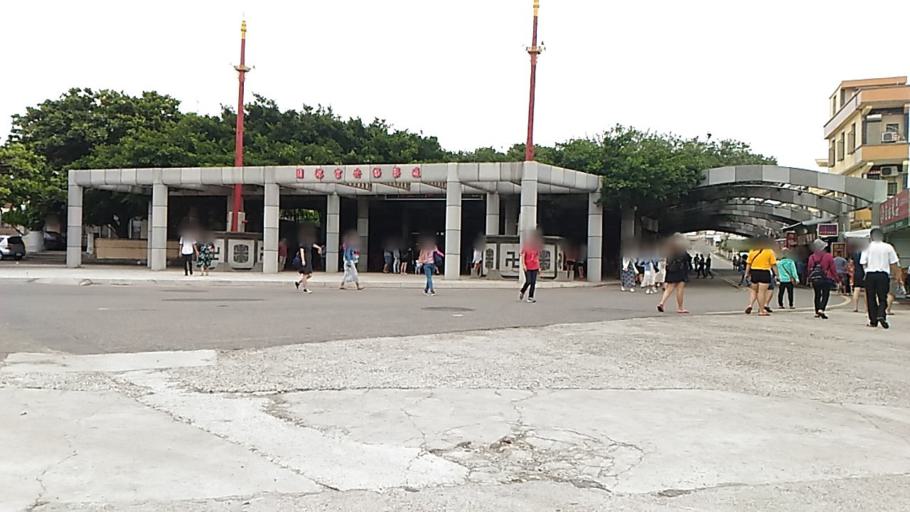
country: TW
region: Taiwan
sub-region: Penghu
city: Ma-kung
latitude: 23.6562
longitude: 119.5571
